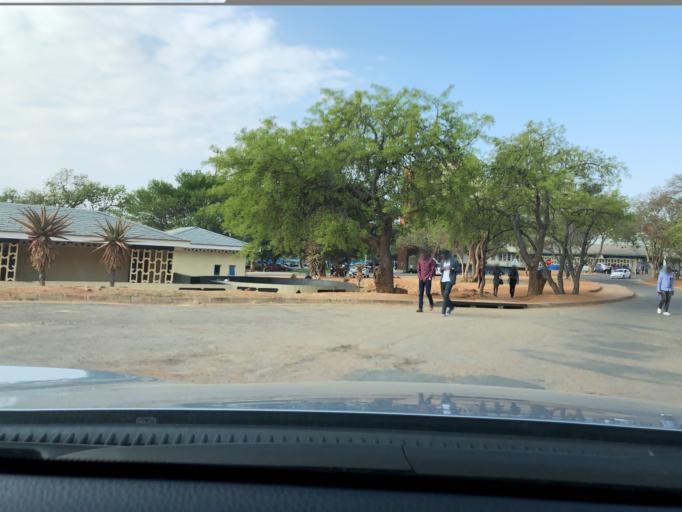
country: ZA
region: Limpopo
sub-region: Capricorn District Municipality
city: Mankoeng
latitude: -23.8887
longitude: 29.7370
